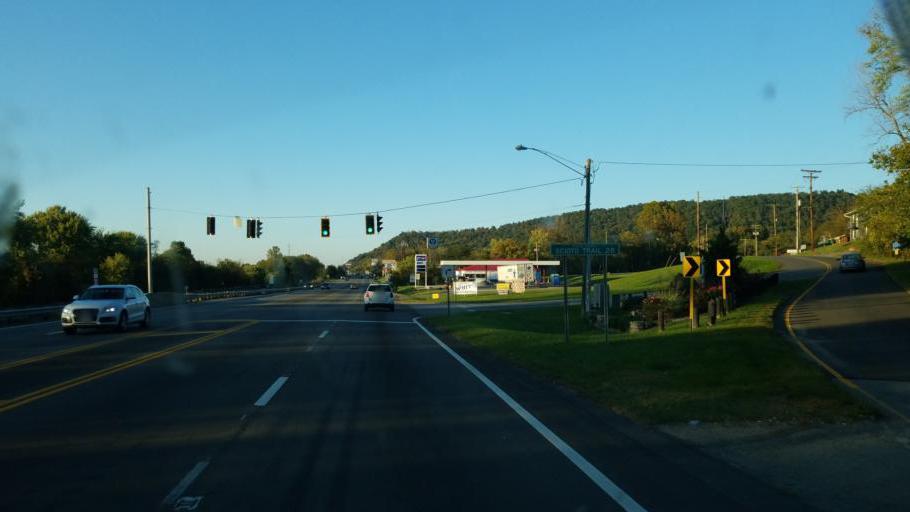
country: US
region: Ohio
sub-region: Scioto County
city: Rosemount
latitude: 38.7796
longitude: -82.9850
